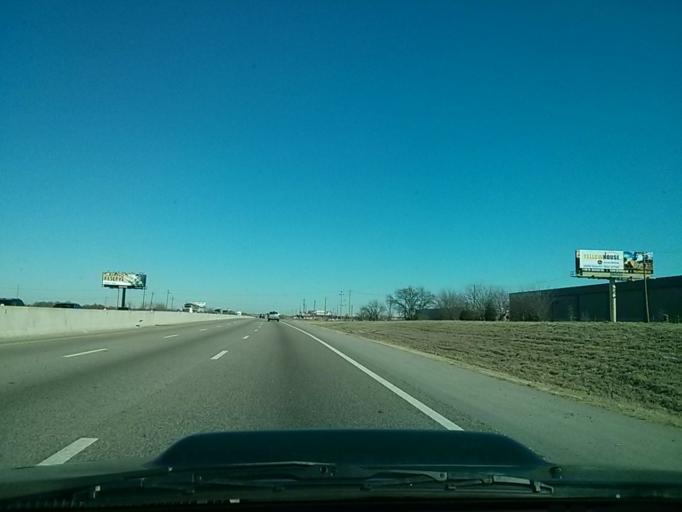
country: US
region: Oklahoma
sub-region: Tulsa County
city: Owasso
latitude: 36.1891
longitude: -95.8513
